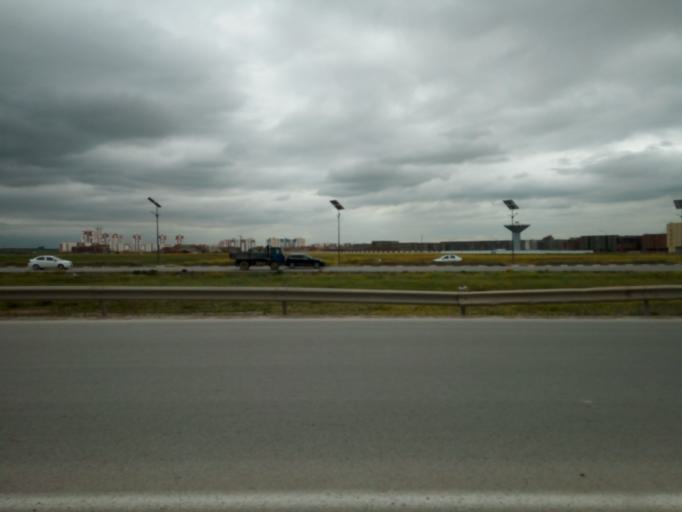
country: DZ
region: Setif
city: El Eulma
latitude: 36.1738
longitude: 5.6737
